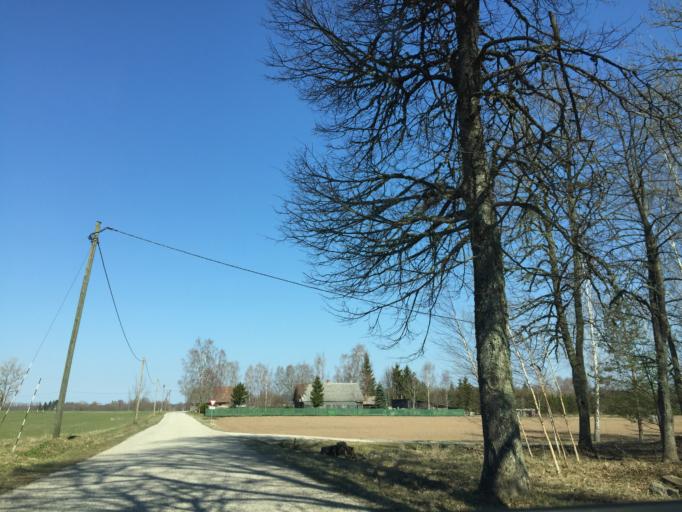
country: EE
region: Tartu
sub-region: Tartu linn
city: Tartu
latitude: 58.5011
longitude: 26.8791
